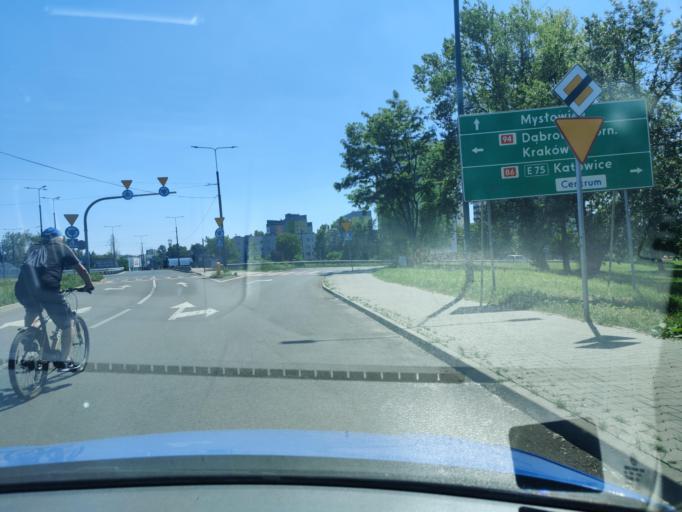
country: PL
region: Silesian Voivodeship
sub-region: Powiat bedzinski
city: Bedzin
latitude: 50.2879
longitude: 19.1486
